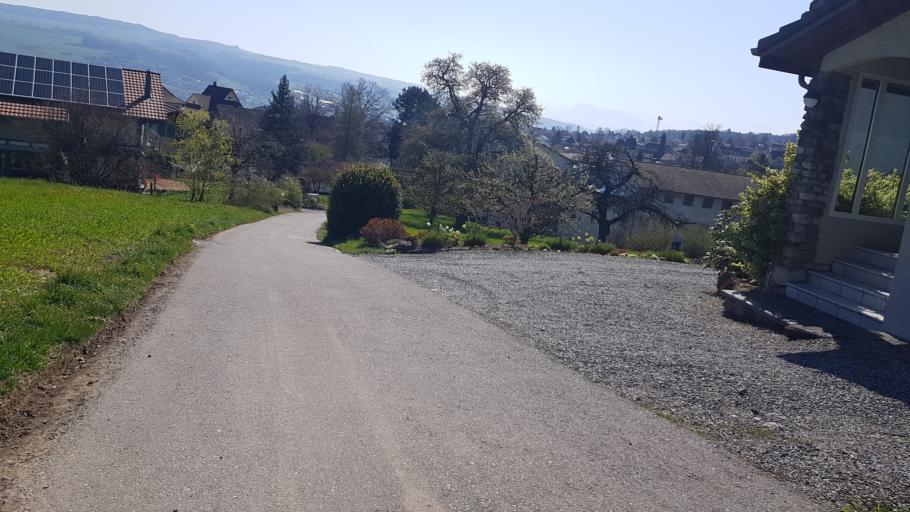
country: CH
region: Aargau
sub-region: Bezirk Kulm
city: Reinach
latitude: 47.2686
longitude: 8.1978
